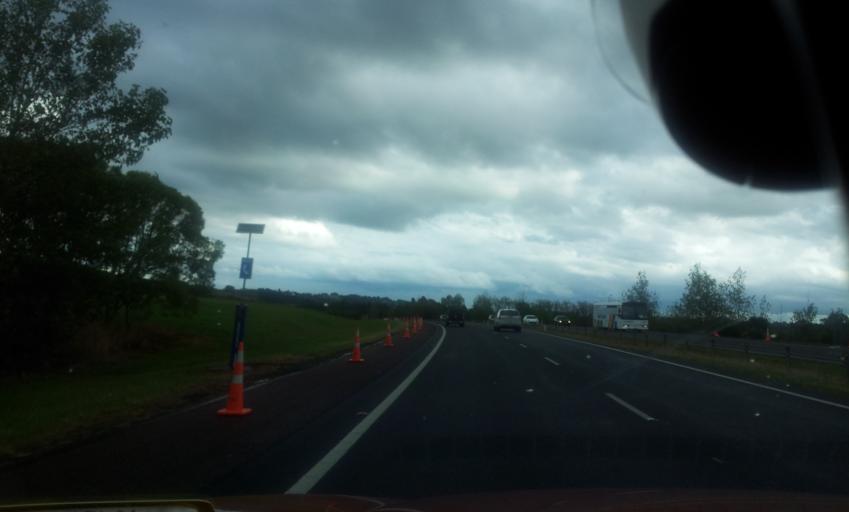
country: NZ
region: Auckland
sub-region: Auckland
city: Rothesay Bay
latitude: -36.6100
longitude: 174.6601
